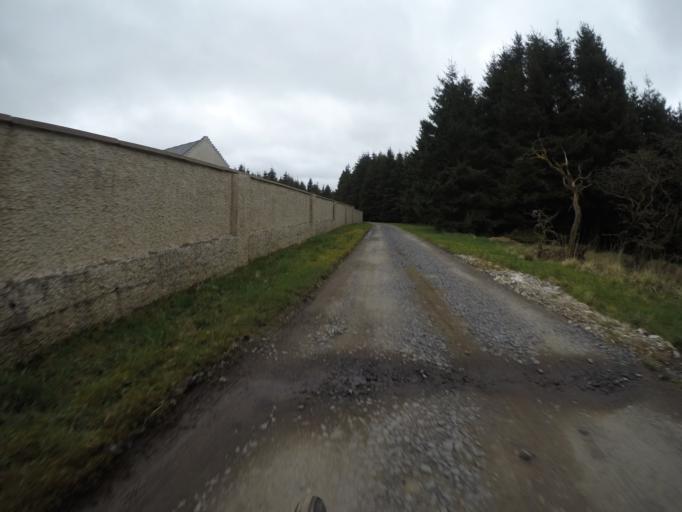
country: GB
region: Scotland
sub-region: East Ayrshire
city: Galston
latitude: 55.6768
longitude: -4.3671
